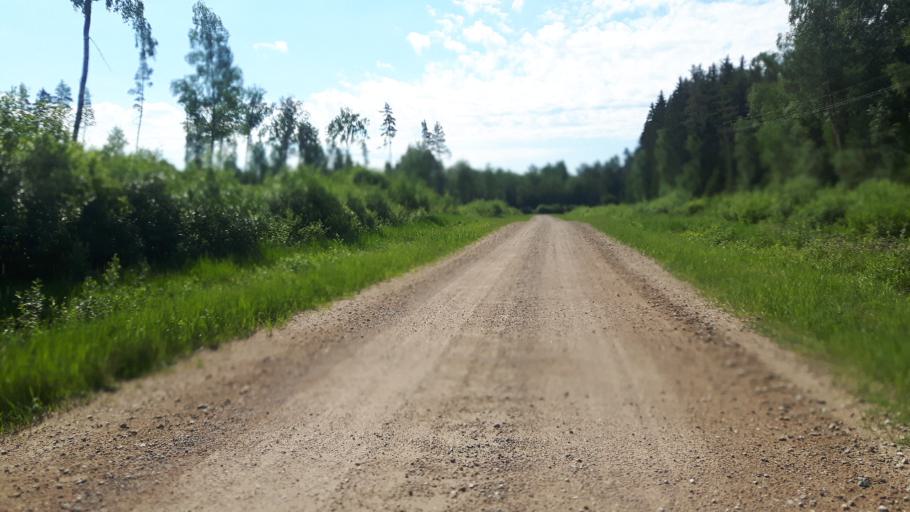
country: EE
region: Paernumaa
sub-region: Vaendra vald (alev)
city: Vandra
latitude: 58.6936
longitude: 25.0327
